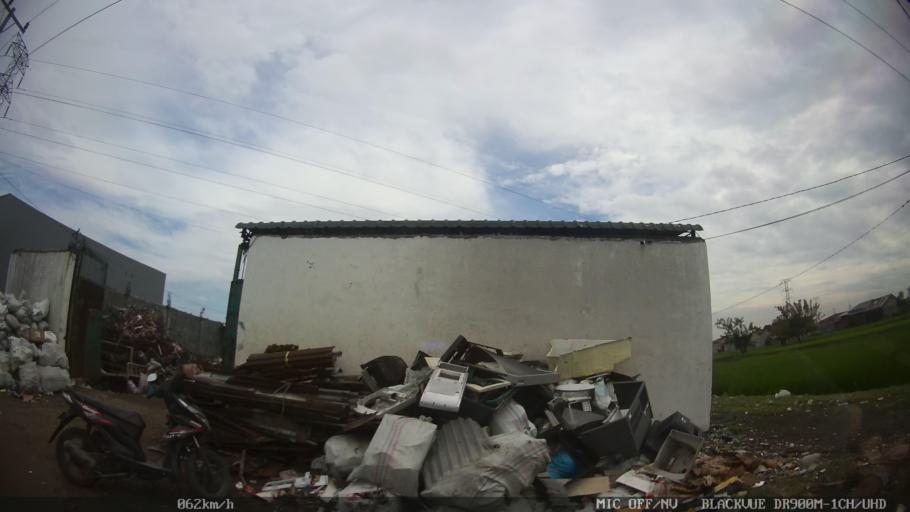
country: ID
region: North Sumatra
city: Sunggal
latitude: 3.6144
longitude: 98.5921
